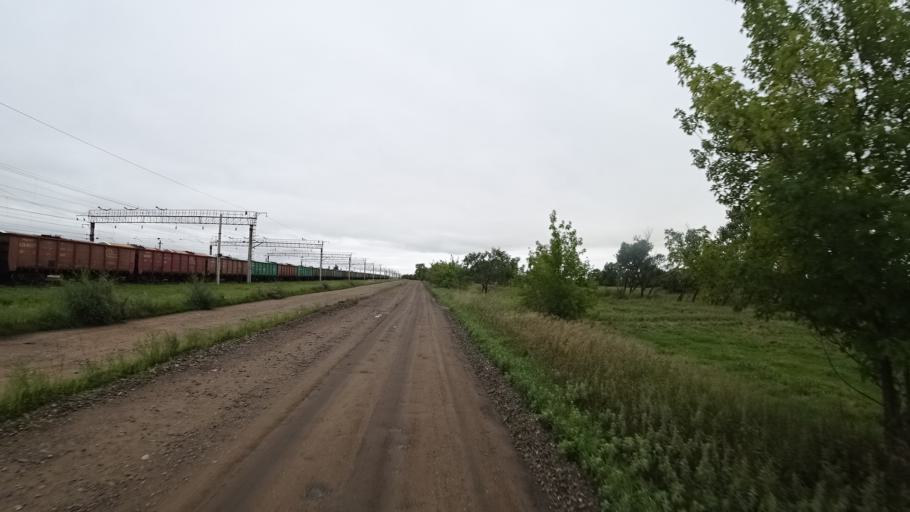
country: RU
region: Primorskiy
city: Chernigovka
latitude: 44.3402
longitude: 132.5329
